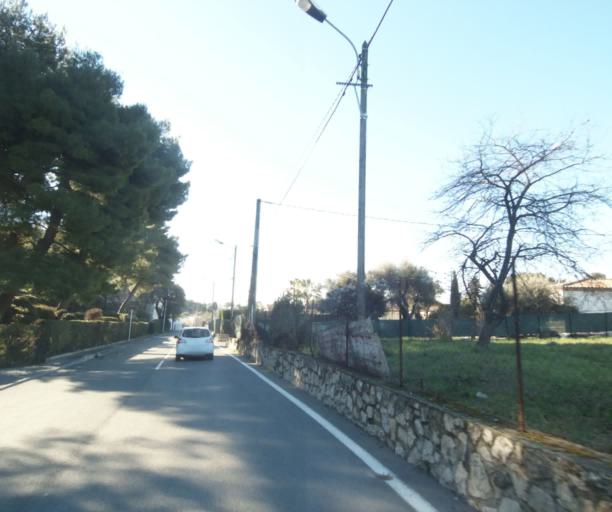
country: FR
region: Provence-Alpes-Cote d'Azur
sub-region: Departement des Alpes-Maritimes
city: Antibes
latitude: 43.5810
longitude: 7.0944
